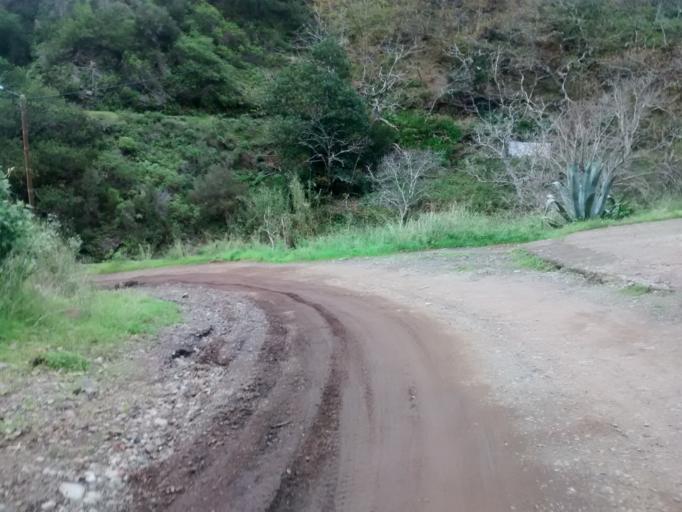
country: PT
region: Madeira
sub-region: Camara de Lobos
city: Curral das Freiras
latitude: 32.7269
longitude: -17.0062
